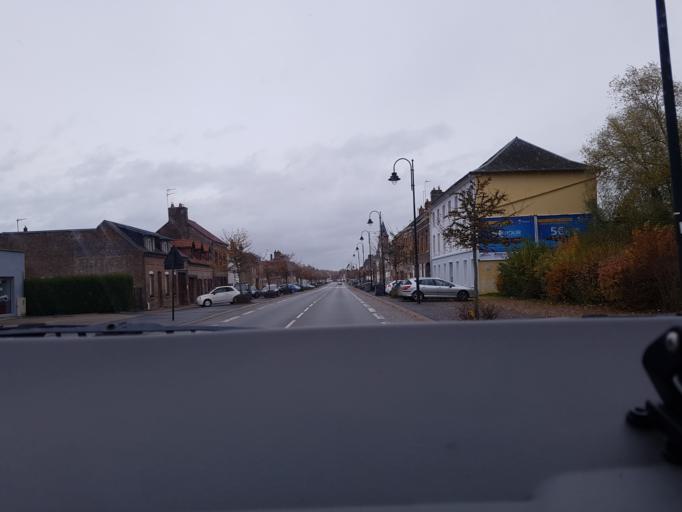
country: FR
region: Picardie
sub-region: Departement de la Somme
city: Abbeville
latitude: 50.1073
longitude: 1.8032
